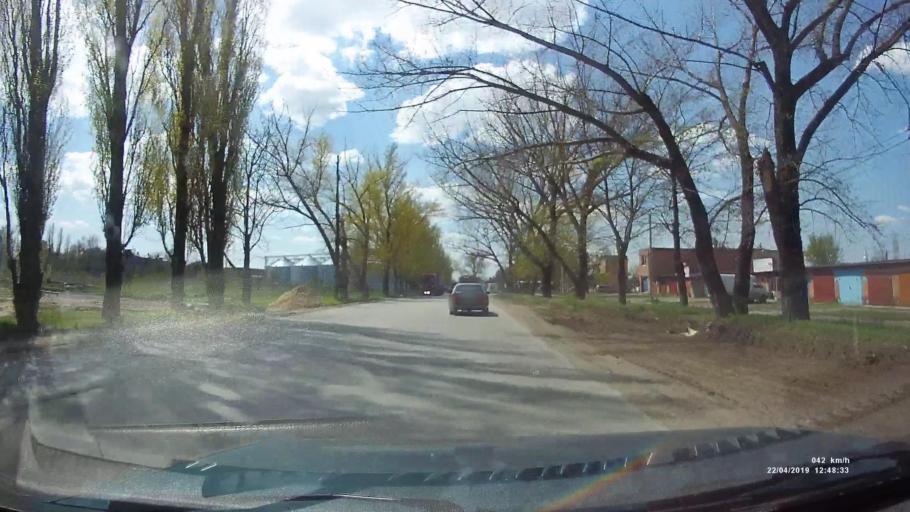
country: RU
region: Rostov
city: Azov
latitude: 47.0953
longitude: 39.4034
